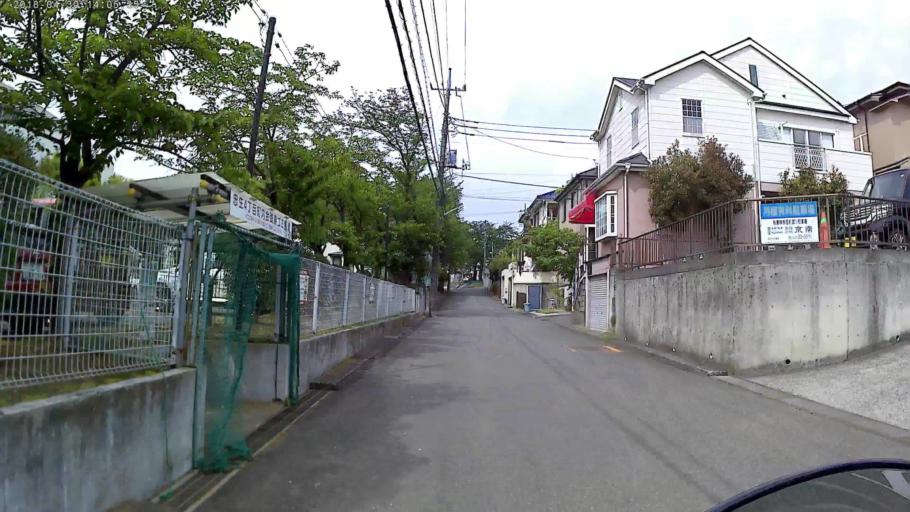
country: JP
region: Tokyo
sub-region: Machida-shi
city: Machida
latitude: 35.5824
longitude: 139.4087
